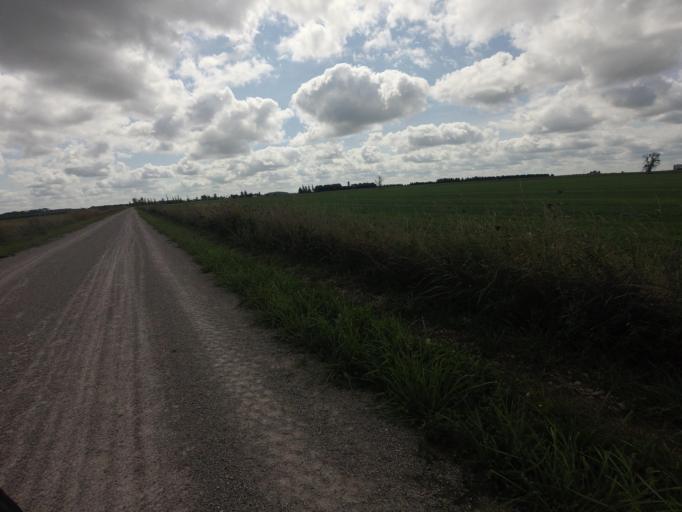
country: CA
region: Ontario
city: Huron East
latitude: 43.6087
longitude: -81.1266
